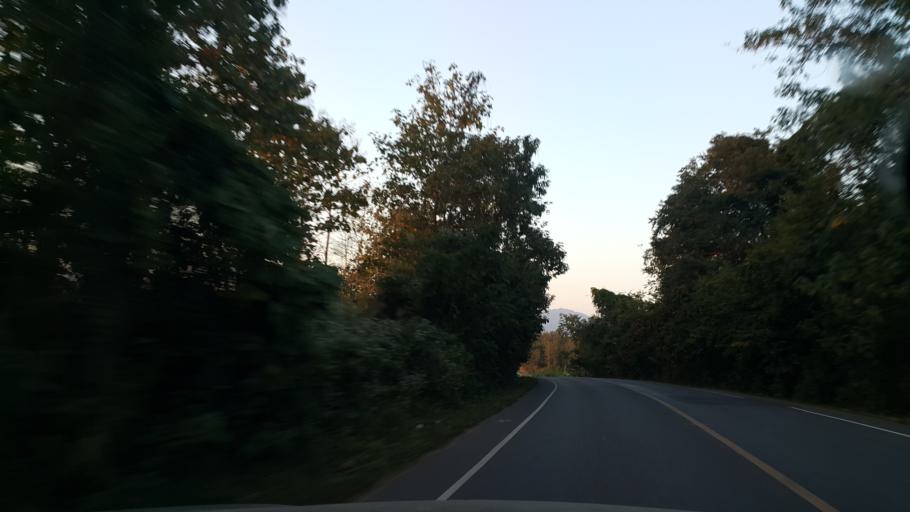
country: TH
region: Phrae
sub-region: Amphoe Wang Chin
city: Wang Chin
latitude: 17.8542
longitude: 99.6276
